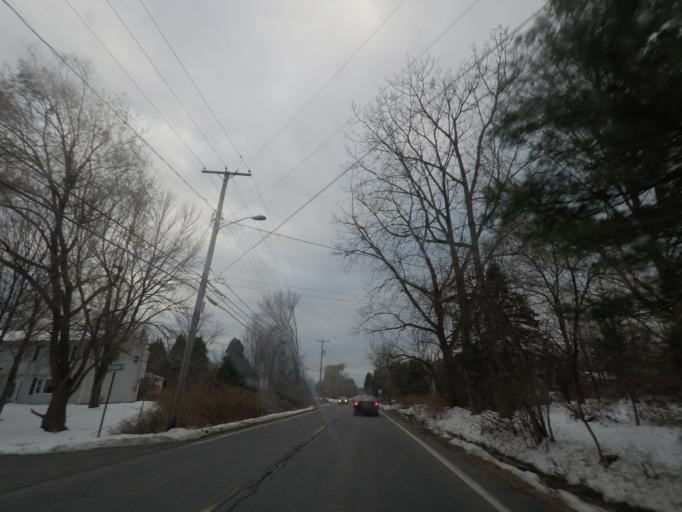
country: US
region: New York
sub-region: Ulster County
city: New Paltz
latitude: 41.7062
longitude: -74.0927
